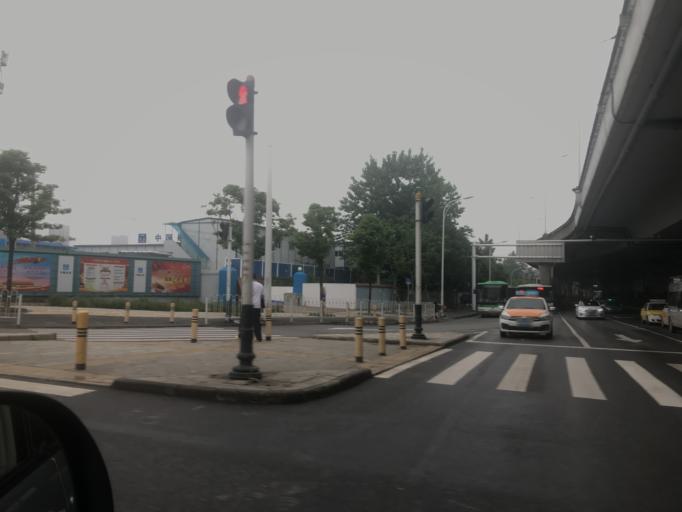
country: CN
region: Hubei
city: Yongfeng
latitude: 30.5559
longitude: 114.2370
